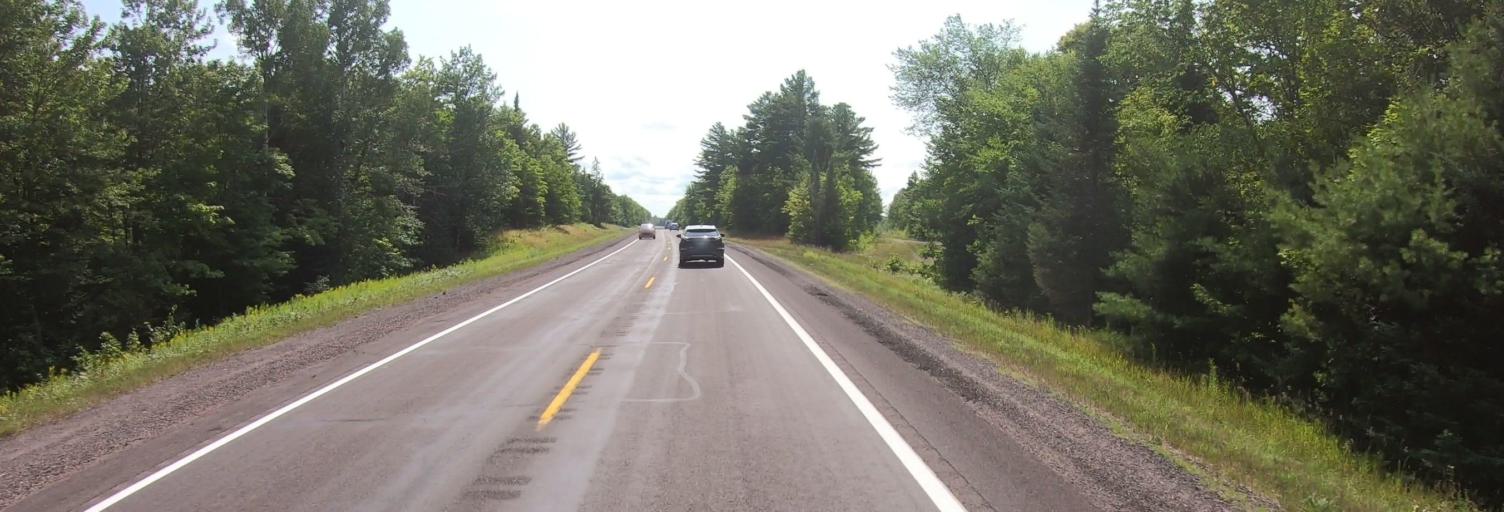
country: US
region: Michigan
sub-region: Houghton County
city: Hancock
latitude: 46.8693
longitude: -88.8977
